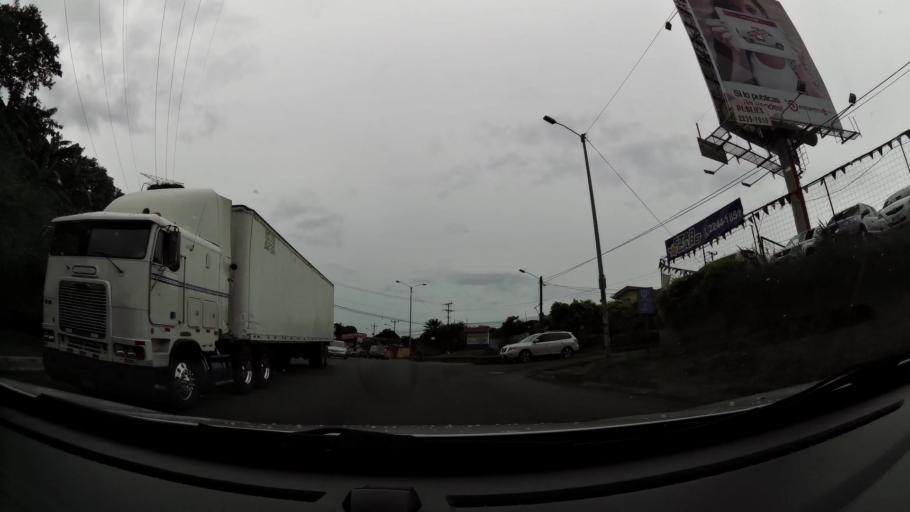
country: CR
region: San Jose
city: San Juan
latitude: 9.9699
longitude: -84.0864
